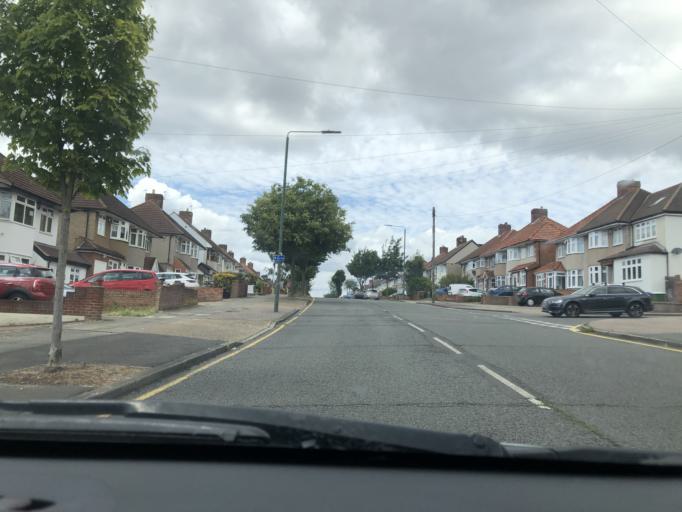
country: GB
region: England
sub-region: Greater London
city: Bexley
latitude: 51.4526
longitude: 0.1486
